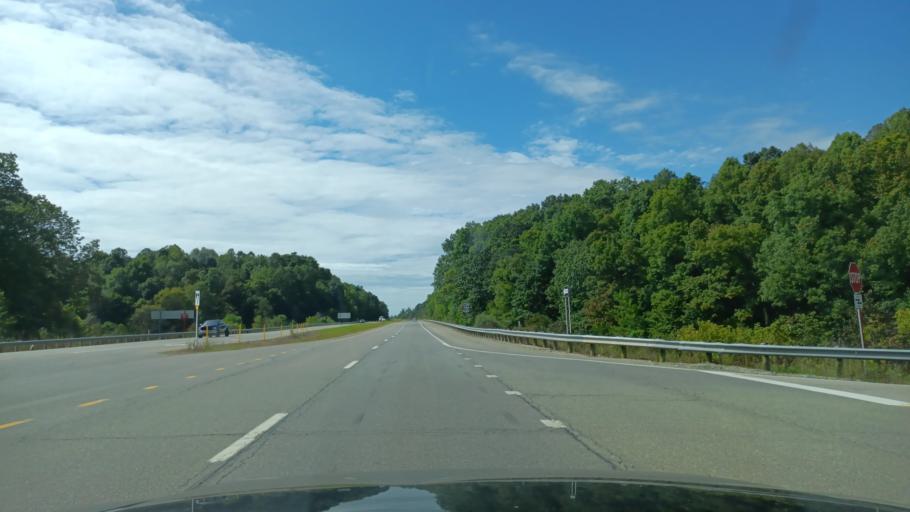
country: US
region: West Virginia
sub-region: Ritchie County
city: Pennsboro
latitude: 39.2743
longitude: -81.0040
